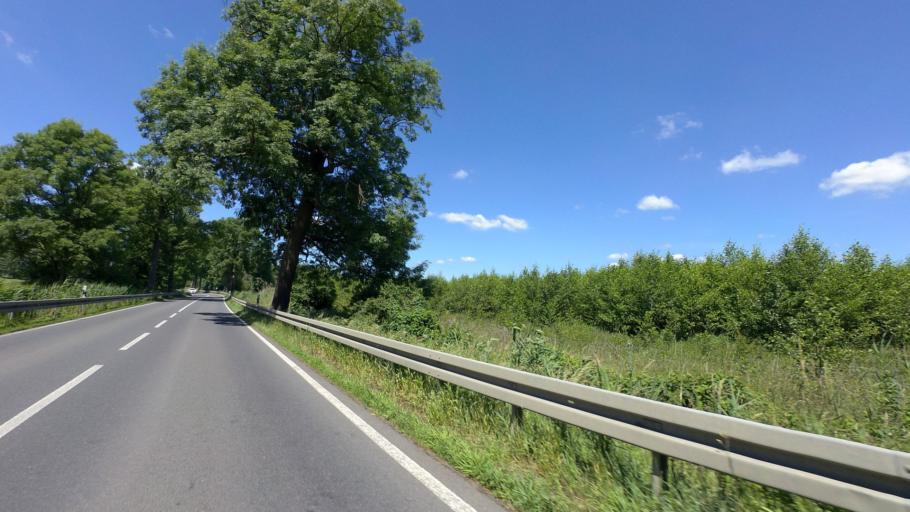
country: DE
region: Brandenburg
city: Golssen
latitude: 51.9620
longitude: 13.6228
